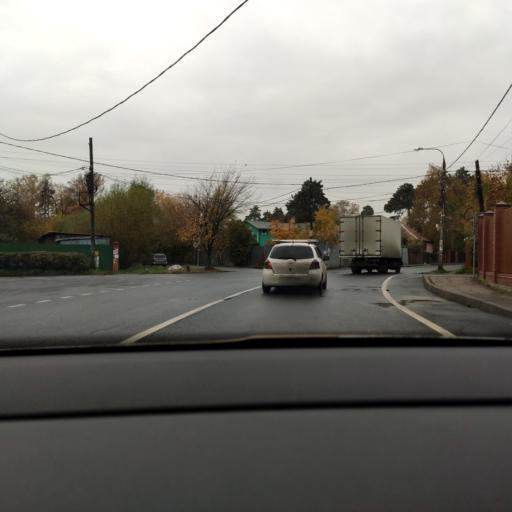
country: RU
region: Moskovskaya
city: Druzhba
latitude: 55.8851
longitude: 37.7415
